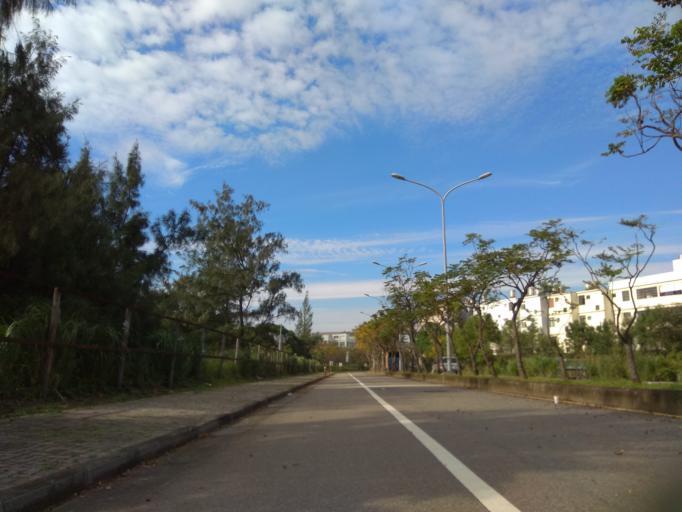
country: TW
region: Taiwan
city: Taoyuan City
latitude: 25.0554
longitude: 121.1812
